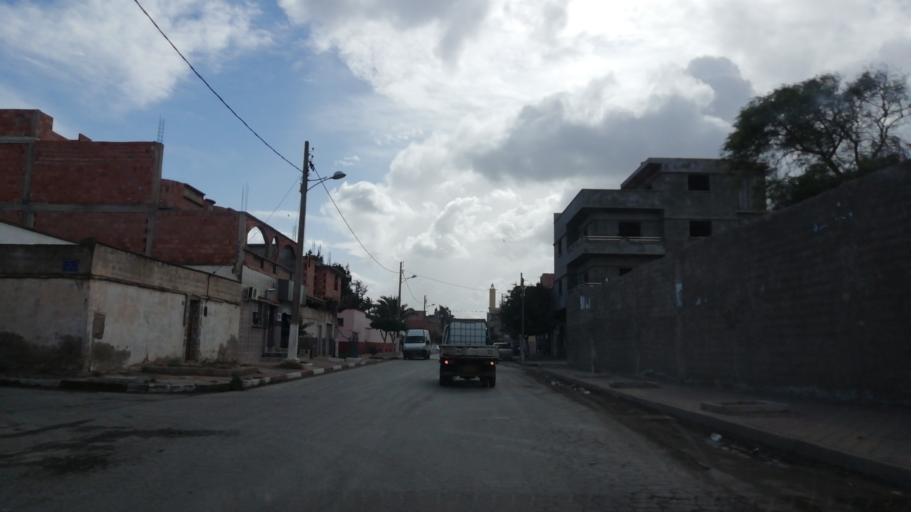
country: DZ
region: Oran
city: Sidi ech Chahmi
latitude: 35.6397
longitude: -0.5512
